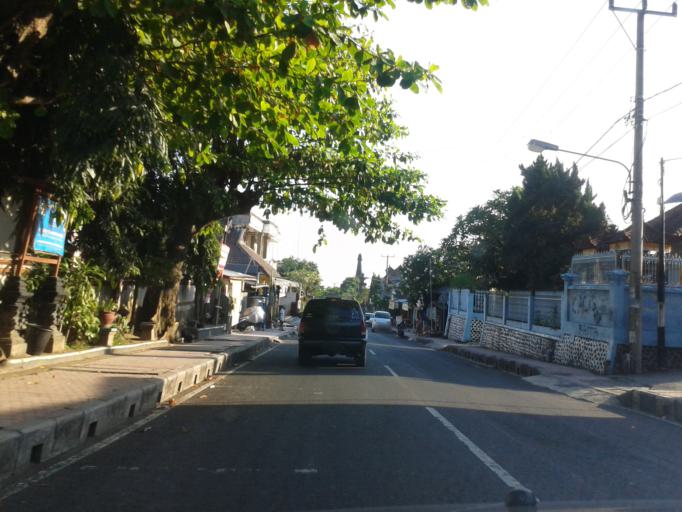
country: ID
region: Bali
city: Semarapura
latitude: -8.5320
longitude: 115.4043
